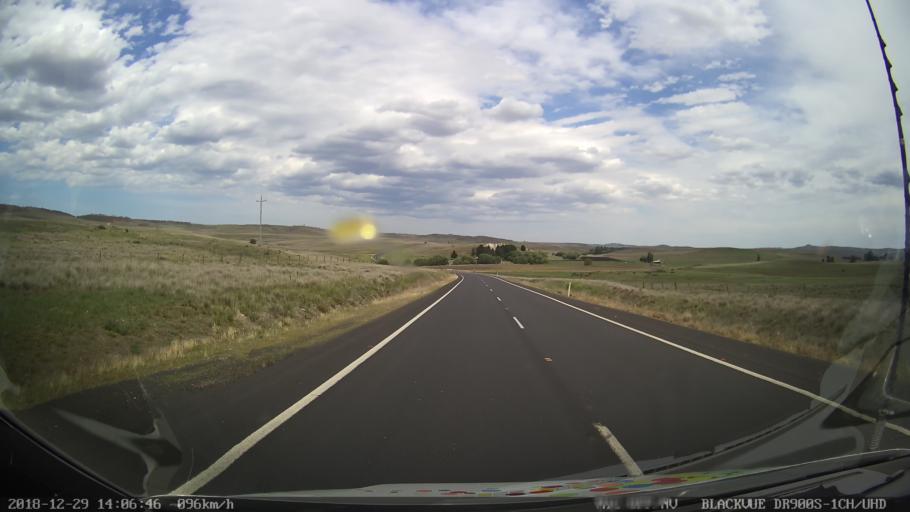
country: AU
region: New South Wales
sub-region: Cooma-Monaro
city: Cooma
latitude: -36.3438
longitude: 149.2072
